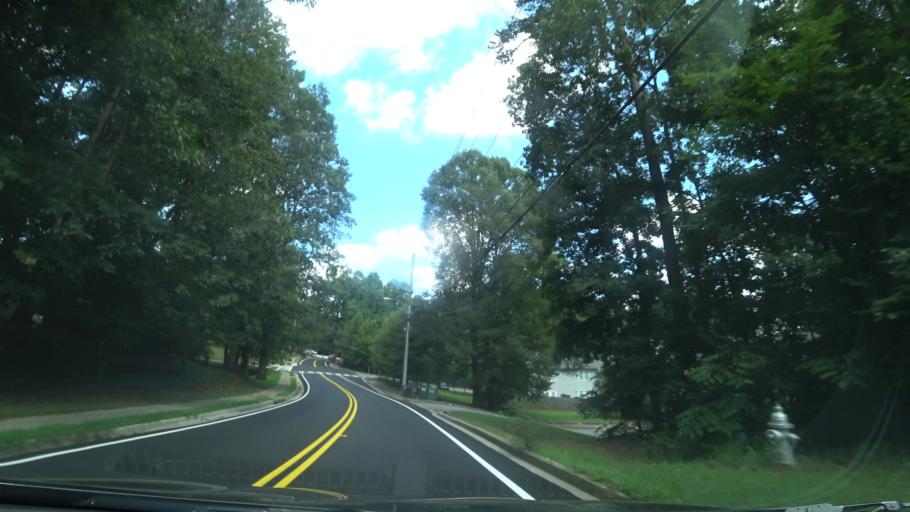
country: US
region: Georgia
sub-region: Gwinnett County
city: Norcross
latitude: 33.9115
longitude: -84.1868
